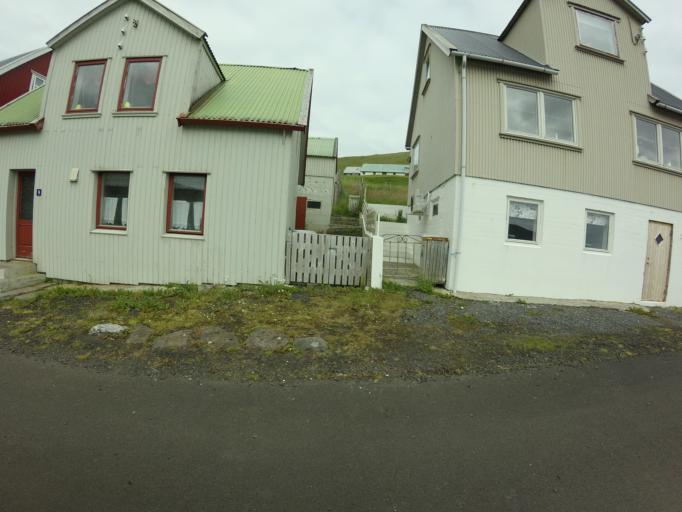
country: FO
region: Suduroy
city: Tvoroyri
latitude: 61.6331
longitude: -6.9274
